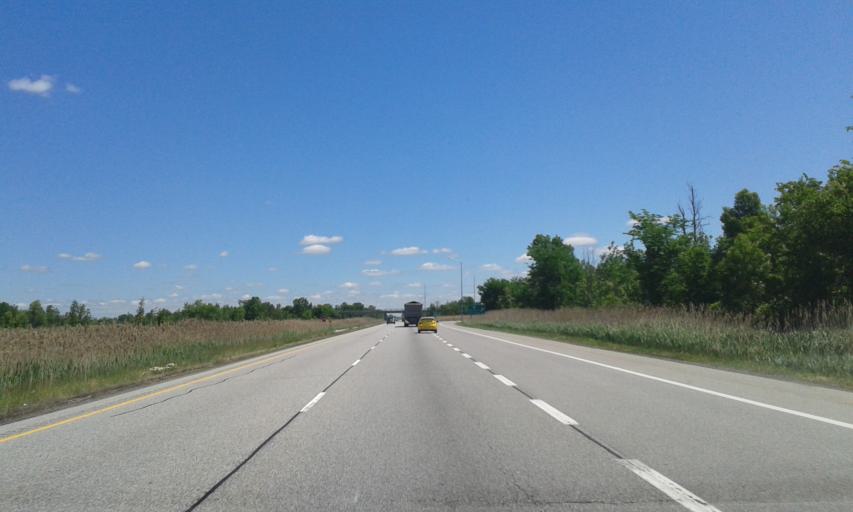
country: US
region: New York
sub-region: St. Lawrence County
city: Norfolk
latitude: 44.9143
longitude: -75.2036
